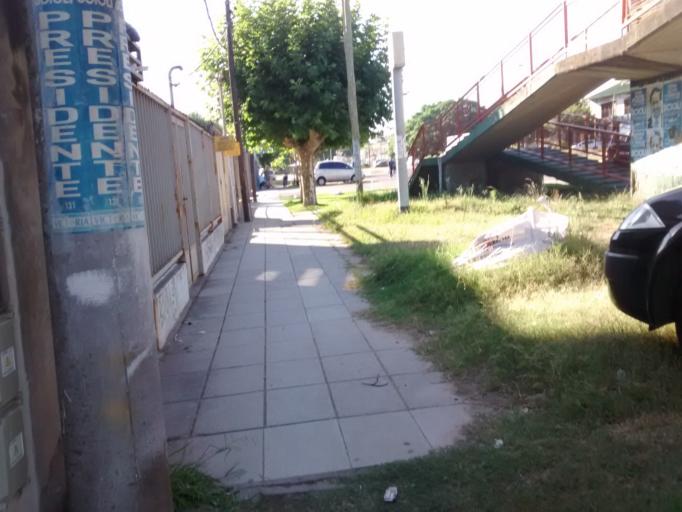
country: AR
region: Buenos Aires
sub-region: Partido de La Plata
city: La Plata
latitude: -34.8541
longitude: -58.0786
